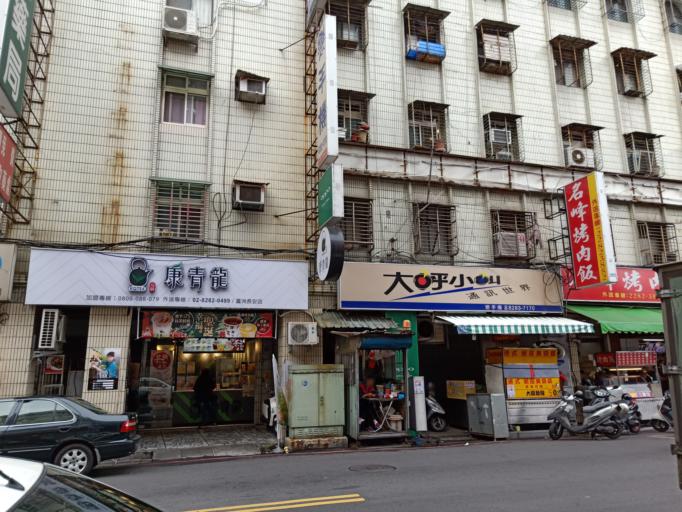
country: TW
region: Taipei
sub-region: Taipei
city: Banqiao
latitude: 25.0805
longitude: 121.4618
